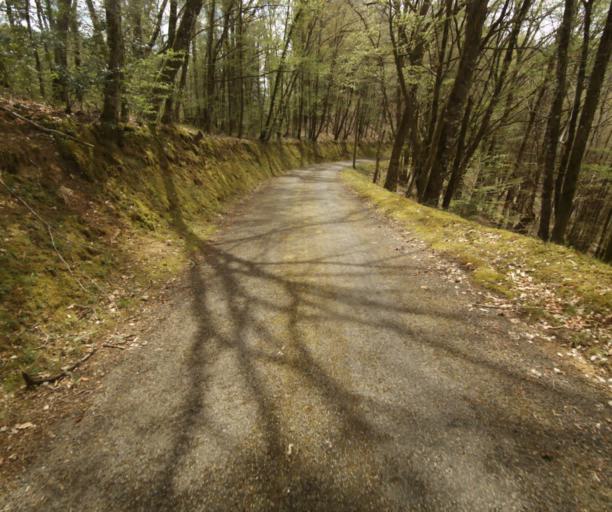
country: FR
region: Limousin
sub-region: Departement de la Correze
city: Sainte-Fortunade
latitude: 45.1907
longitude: 1.8768
